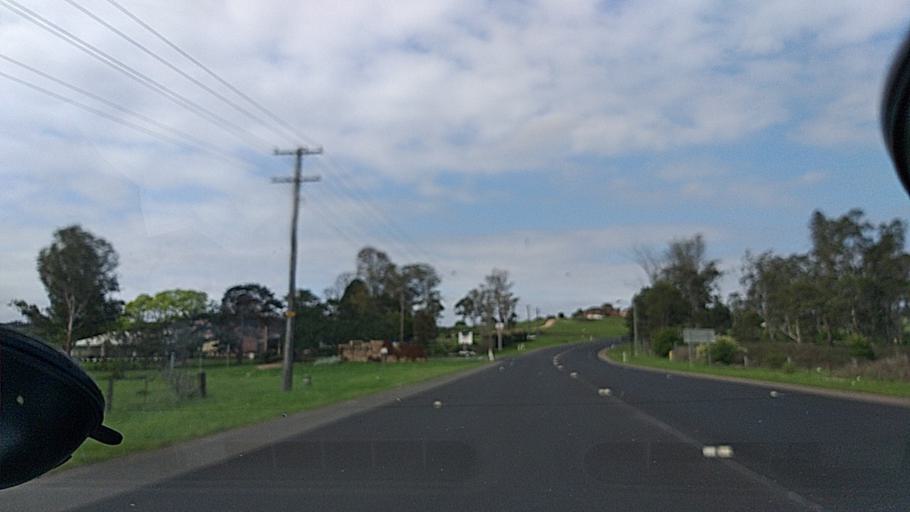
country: AU
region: New South Wales
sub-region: Campbelltown Municipality
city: Glen Alpine
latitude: -34.1100
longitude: 150.7468
